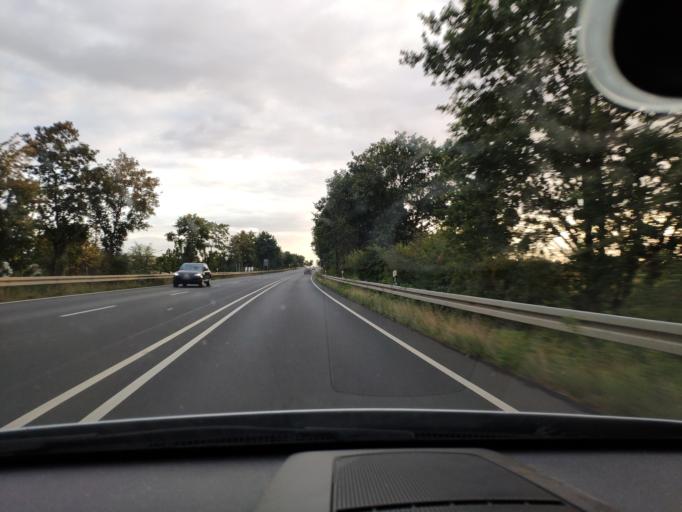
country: DE
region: North Rhine-Westphalia
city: Geilenkirchen
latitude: 50.9771
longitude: 6.0944
